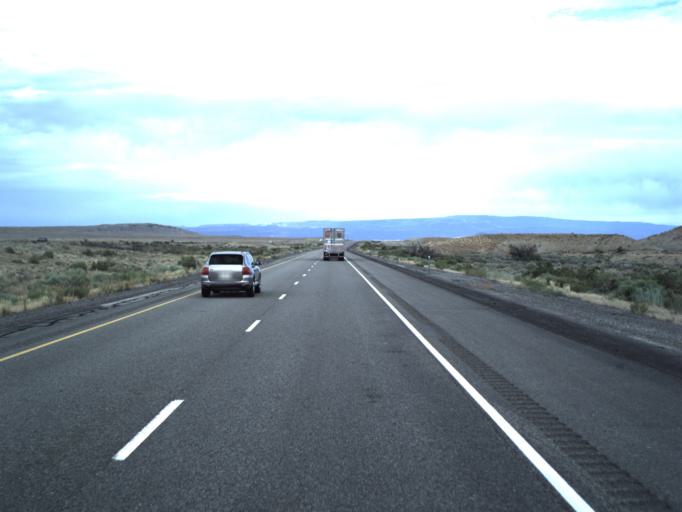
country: US
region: Utah
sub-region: Grand County
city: Moab
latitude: 38.9403
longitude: -109.5218
